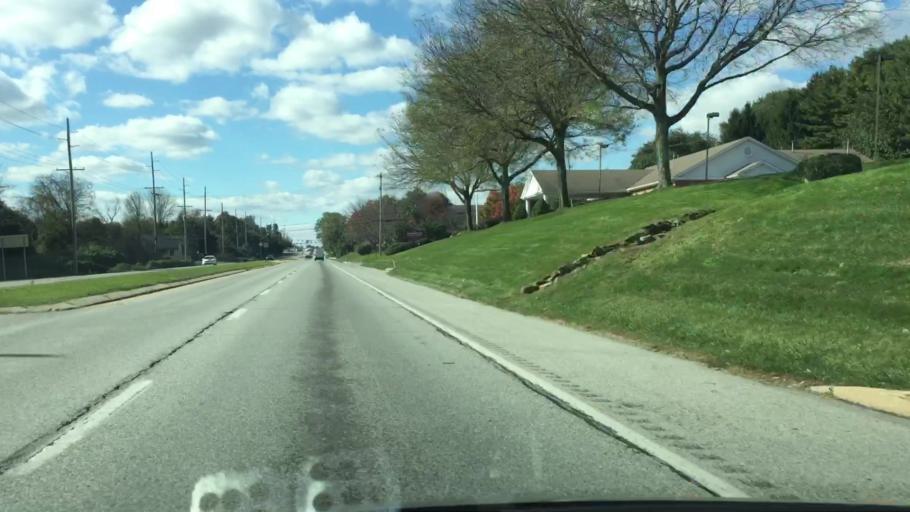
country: US
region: Pennsylvania
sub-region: Chester County
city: Malvern
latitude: 39.9660
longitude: -75.5131
